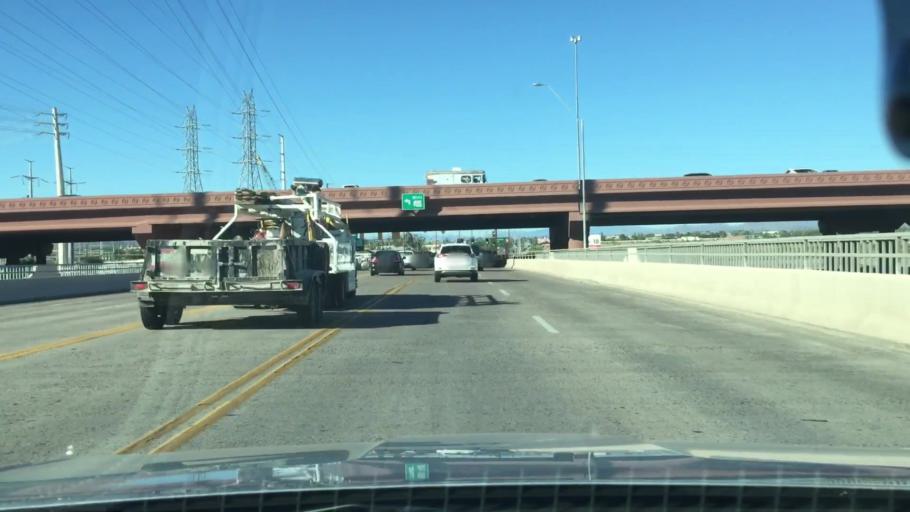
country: US
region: Arizona
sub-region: Maricopa County
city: Tempe
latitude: 33.4349
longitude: -111.9100
